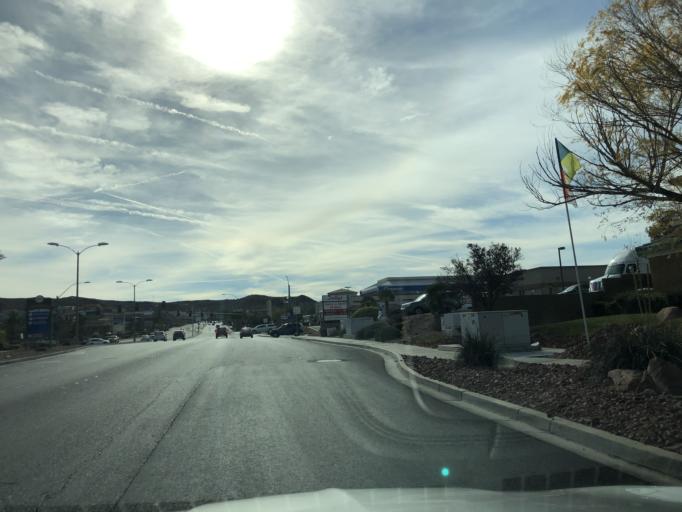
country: US
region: Nevada
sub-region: Clark County
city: Whitney
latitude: 36.0070
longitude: -115.0833
